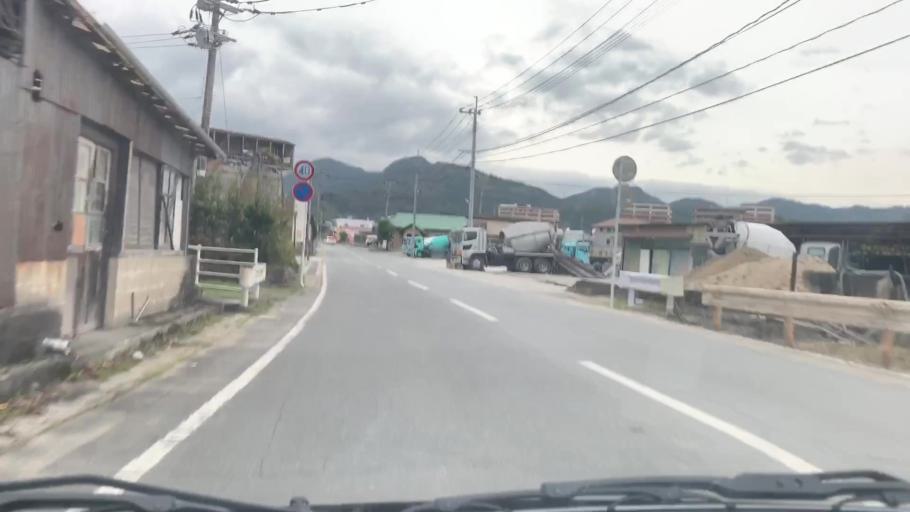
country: JP
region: Saga Prefecture
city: Takeocho-takeo
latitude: 33.1901
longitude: 130.0262
